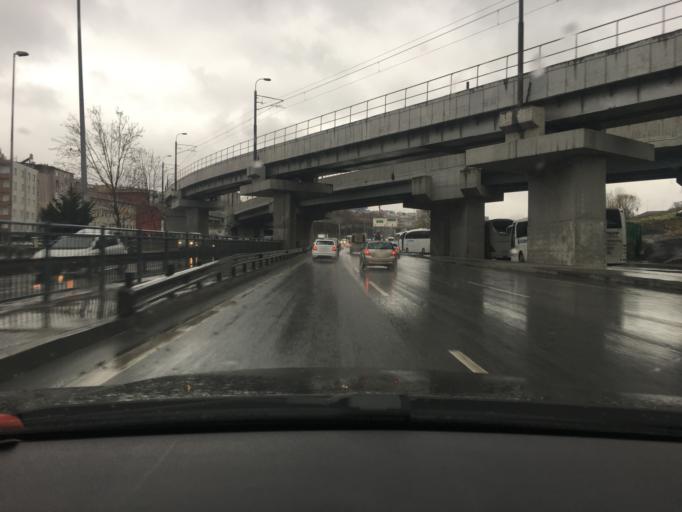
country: TR
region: Istanbul
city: Esenler
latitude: 41.0365
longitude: 28.8924
